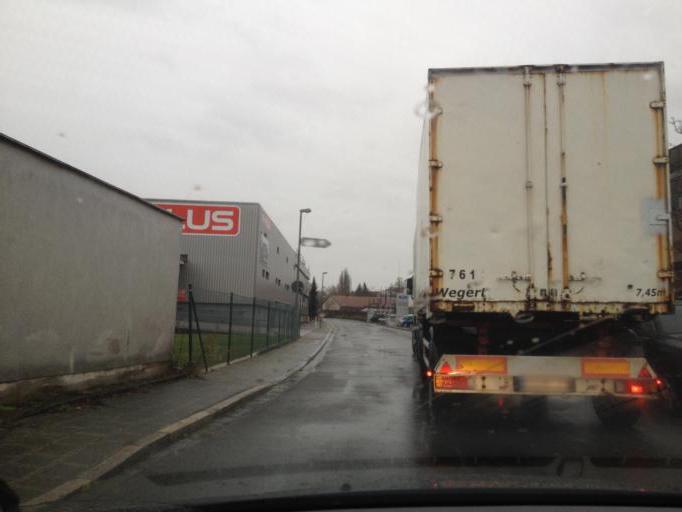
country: DE
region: Bavaria
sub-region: Regierungsbezirk Mittelfranken
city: Lauf an der Pegnitz
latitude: 49.5047
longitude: 11.2709
